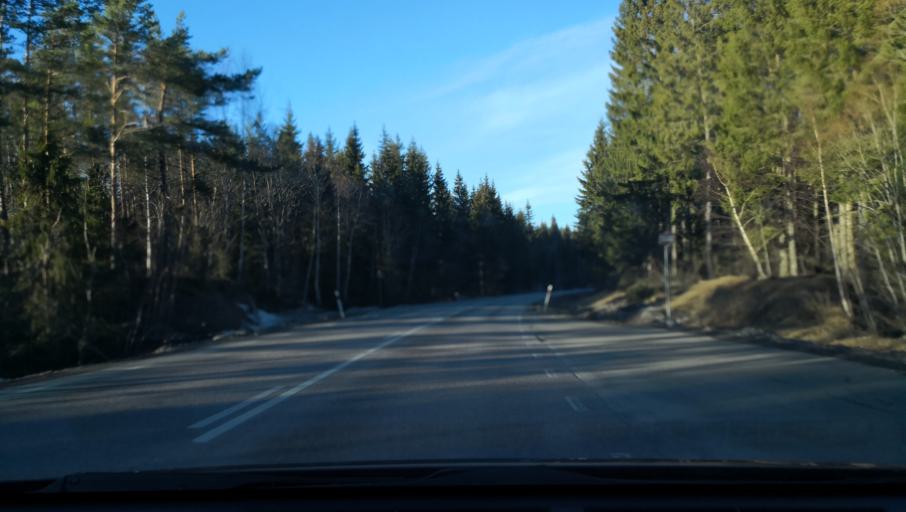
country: SE
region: Uppsala
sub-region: Osthammars Kommun
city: Gimo
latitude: 60.2106
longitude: 18.1917
